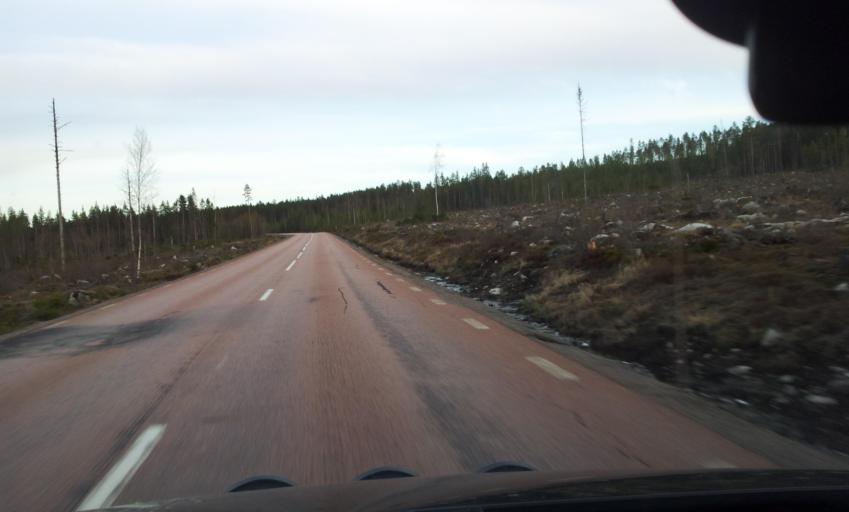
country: SE
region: Gaevleborg
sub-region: Ljusdals Kommun
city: Farila
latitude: 61.9747
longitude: 15.8615
